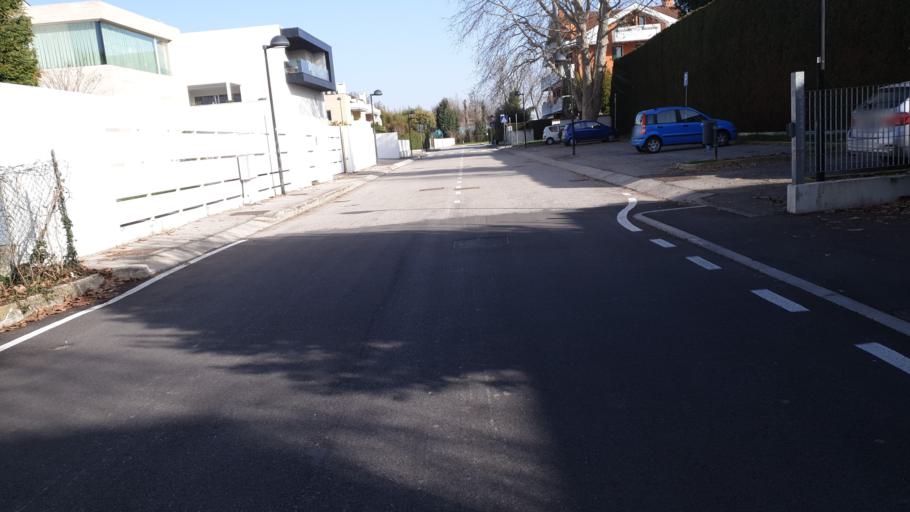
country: IT
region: Veneto
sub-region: Provincia di Padova
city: Noventa
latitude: 45.4170
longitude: 11.9431
